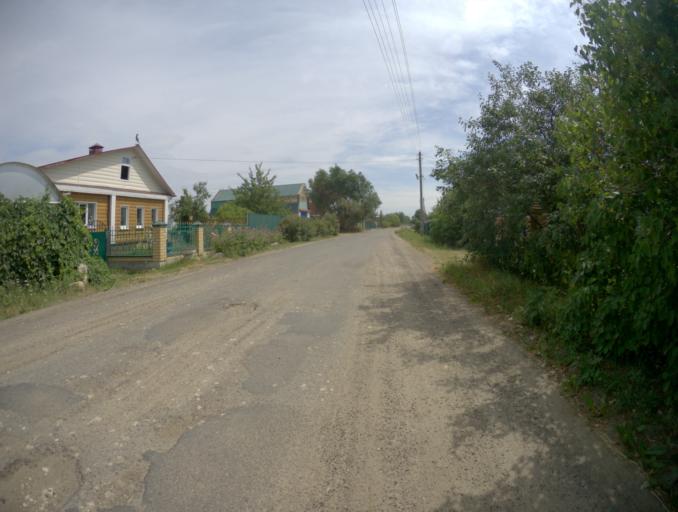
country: RU
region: Vladimir
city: Raduzhnyy
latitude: 56.0251
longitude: 40.3131
